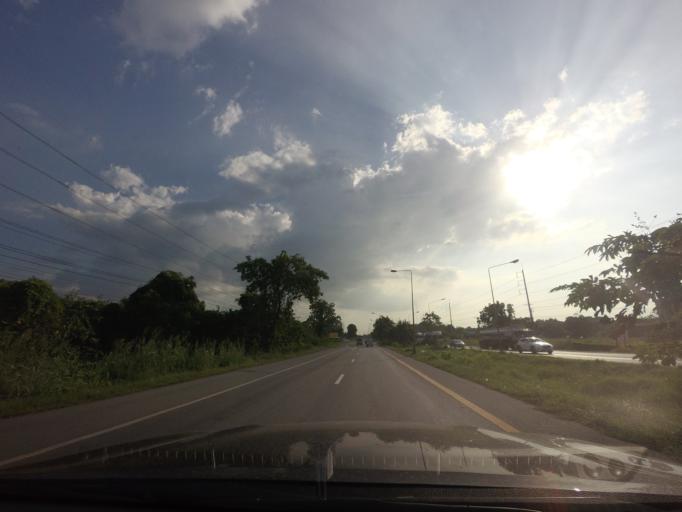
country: TH
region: Sara Buri
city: Saraburi
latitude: 14.5496
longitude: 100.8925
